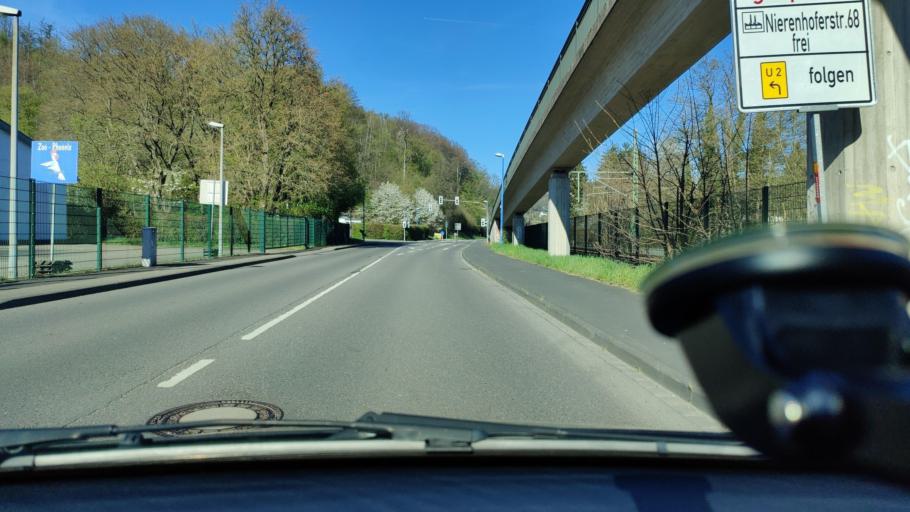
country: DE
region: North Rhine-Westphalia
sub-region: Regierungsbezirk Dusseldorf
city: Velbert
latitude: 51.3485
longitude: 7.1057
